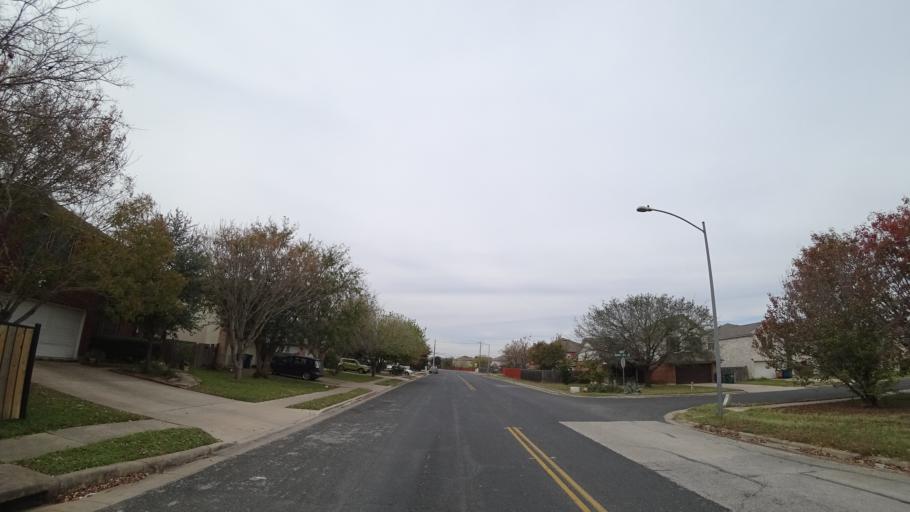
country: US
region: Texas
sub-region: Travis County
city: Onion Creek
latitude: 30.1567
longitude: -97.7397
